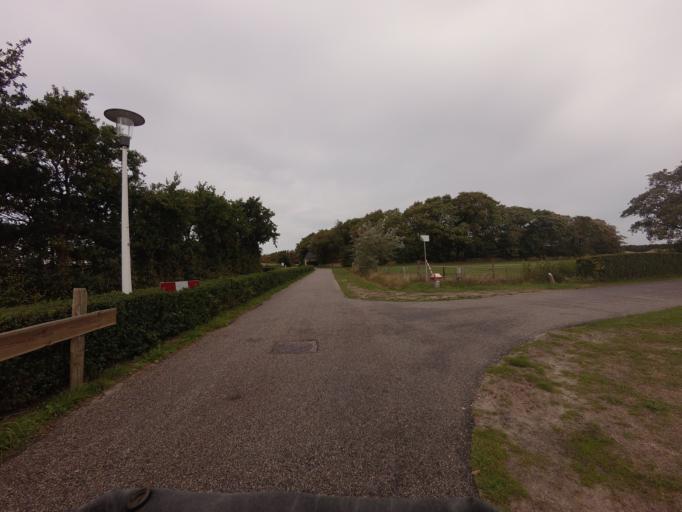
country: NL
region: Friesland
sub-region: Gemeente Ameland
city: Nes
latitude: 53.4474
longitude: 5.7818
